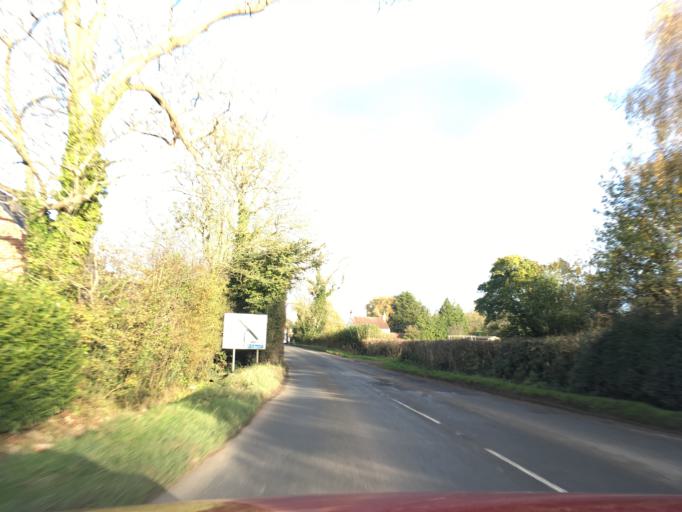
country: GB
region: England
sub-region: Gloucestershire
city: Berkeley
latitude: 51.6915
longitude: -2.4283
